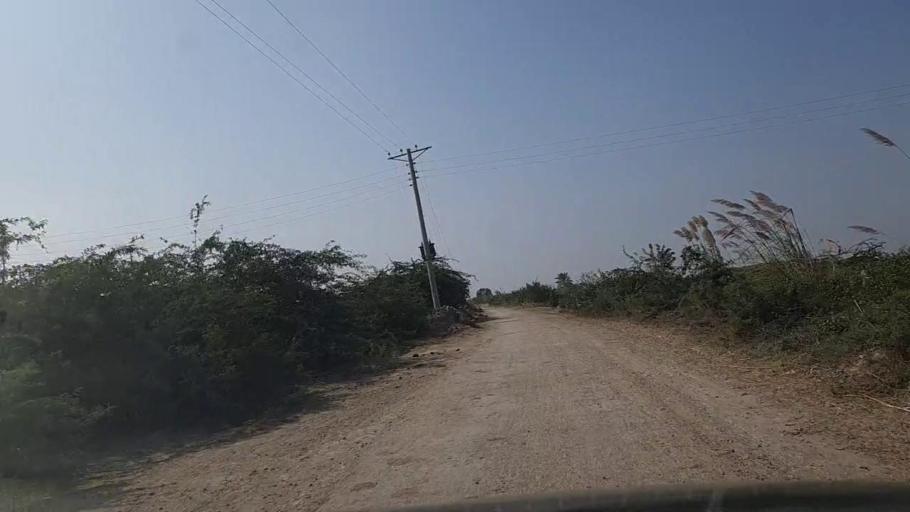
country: PK
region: Sindh
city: Gharo
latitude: 24.6914
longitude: 67.6112
